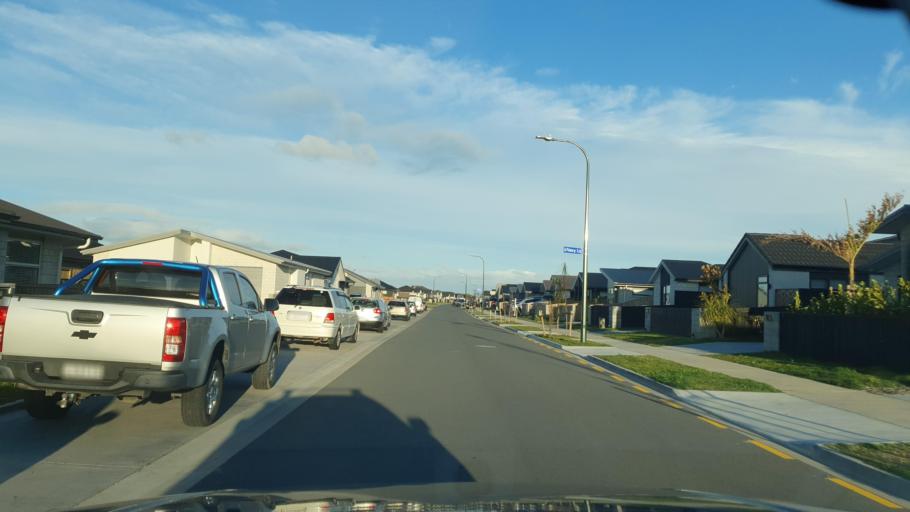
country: NZ
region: Bay of Plenty
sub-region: Western Bay of Plenty District
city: Maketu
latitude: -37.7292
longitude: 176.3366
